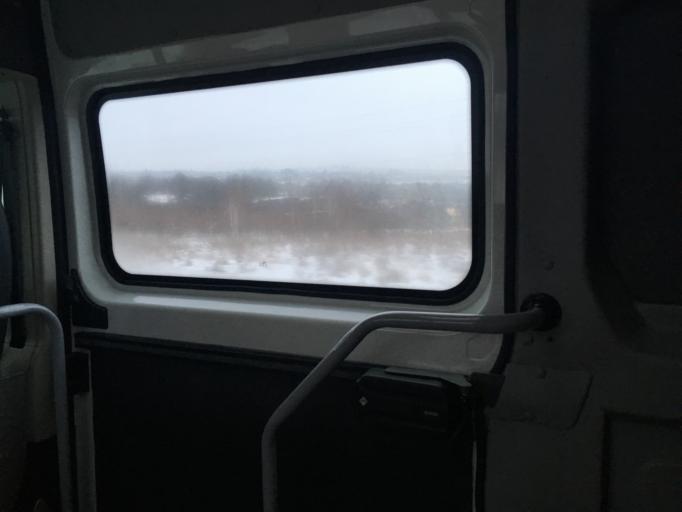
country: RU
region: Tula
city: Dubna
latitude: 54.0943
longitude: 37.0855
